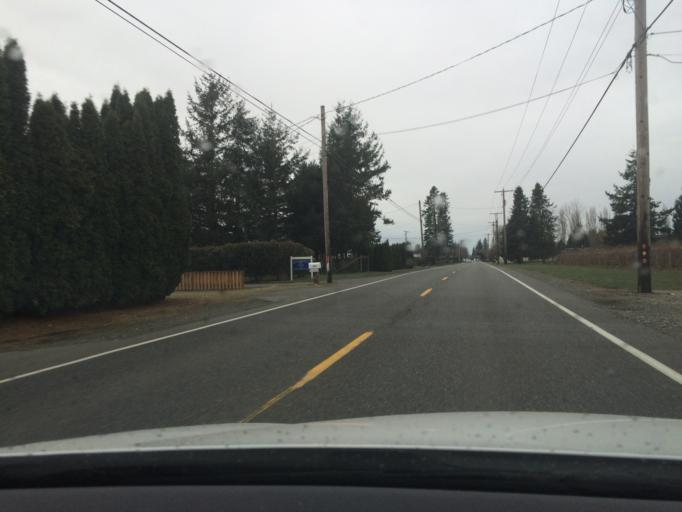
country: US
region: Washington
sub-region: Whatcom County
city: Lynden
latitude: 48.8917
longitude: -122.4660
